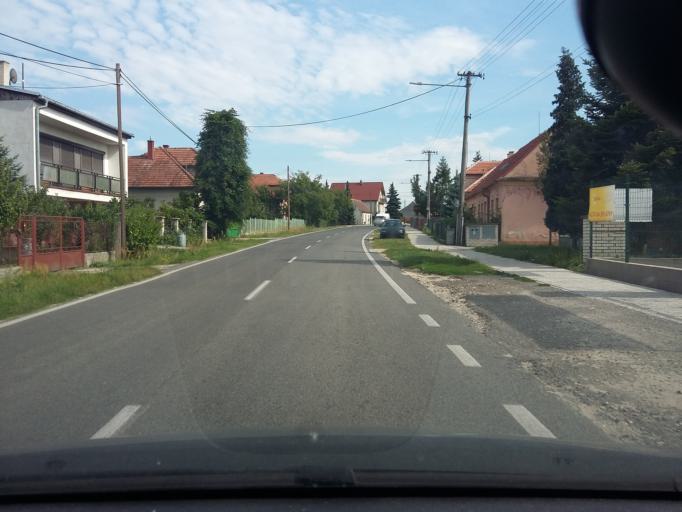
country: SK
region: Trnavsky
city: Gbely
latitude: 48.6335
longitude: 17.2047
